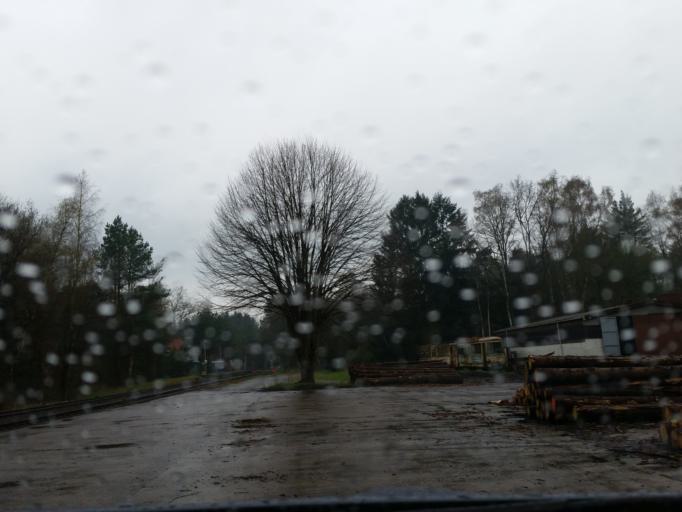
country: DE
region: Lower Saxony
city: Hipstedt
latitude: 53.4987
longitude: 8.9756
